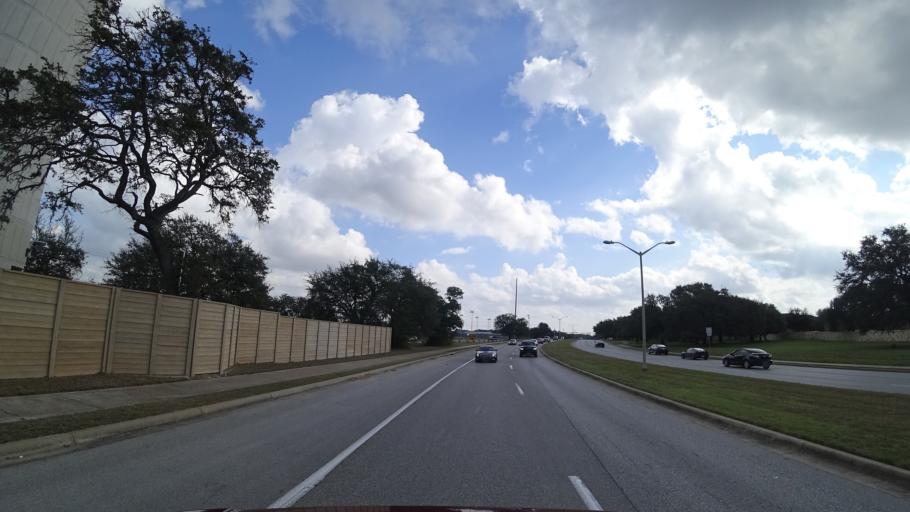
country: US
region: Texas
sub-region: Williamson County
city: Cedar Park
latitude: 30.4717
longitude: -97.8466
